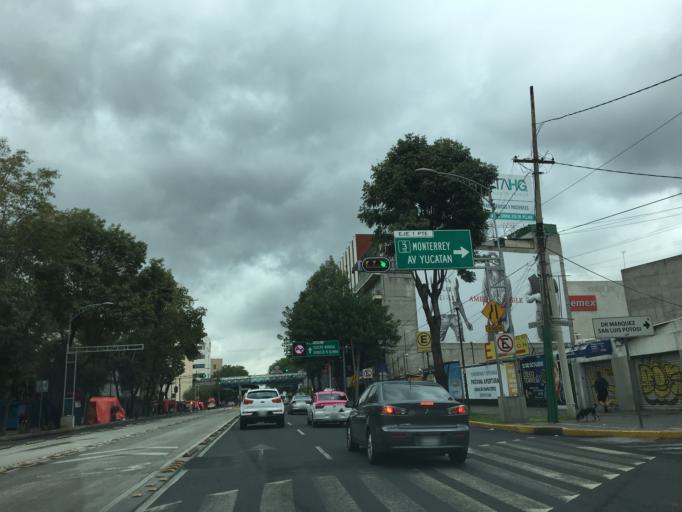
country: MX
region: Mexico City
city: Benito Juarez
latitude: 19.4129
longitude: -99.1547
